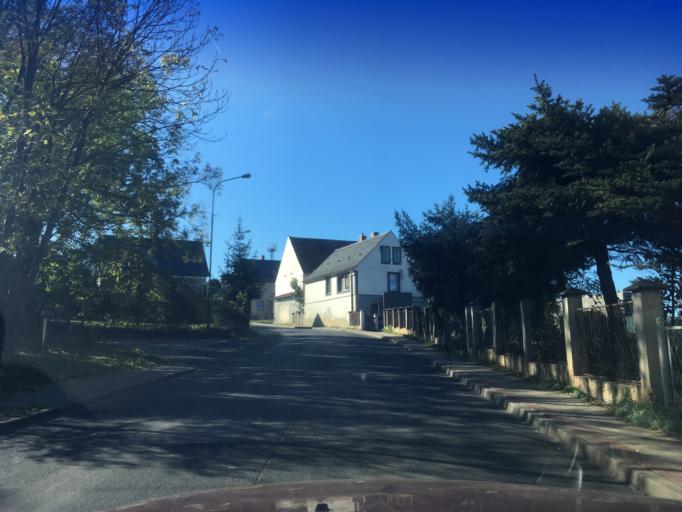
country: DE
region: Saxony
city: Zittau
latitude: 50.8940
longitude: 14.8412
